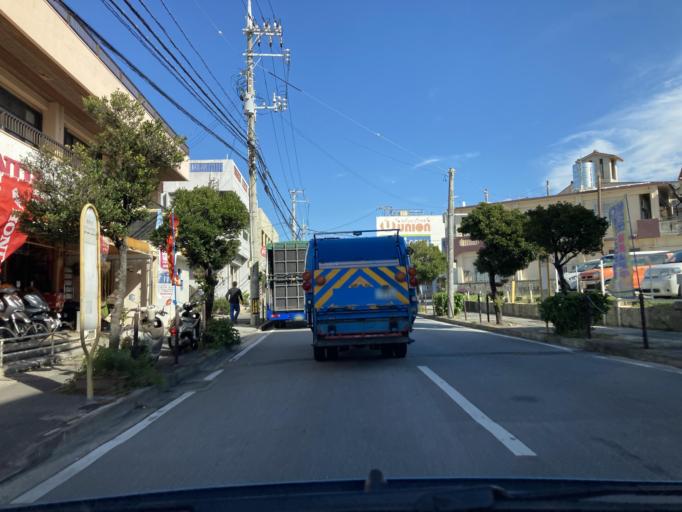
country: JP
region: Okinawa
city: Tomigusuku
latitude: 26.1676
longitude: 127.6942
